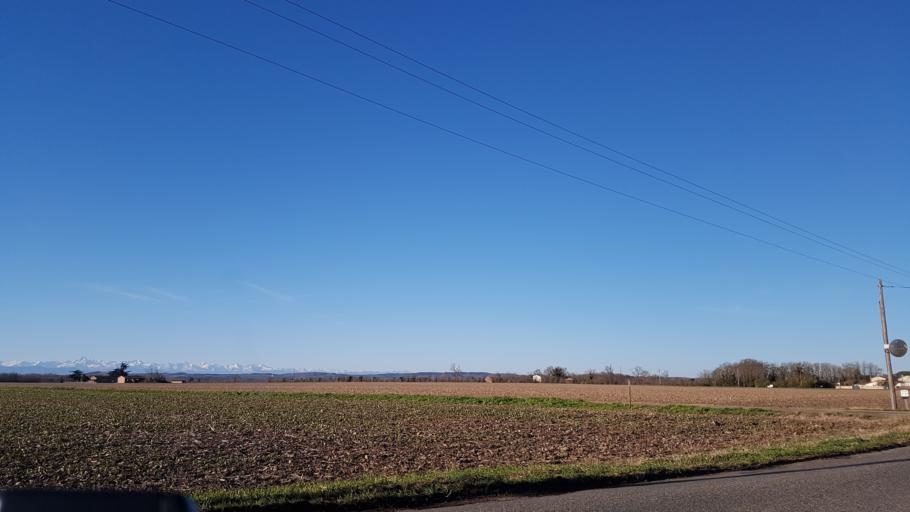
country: FR
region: Midi-Pyrenees
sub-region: Departement de la Haute-Garonne
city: Calmont
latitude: 43.2904
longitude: 1.5944
